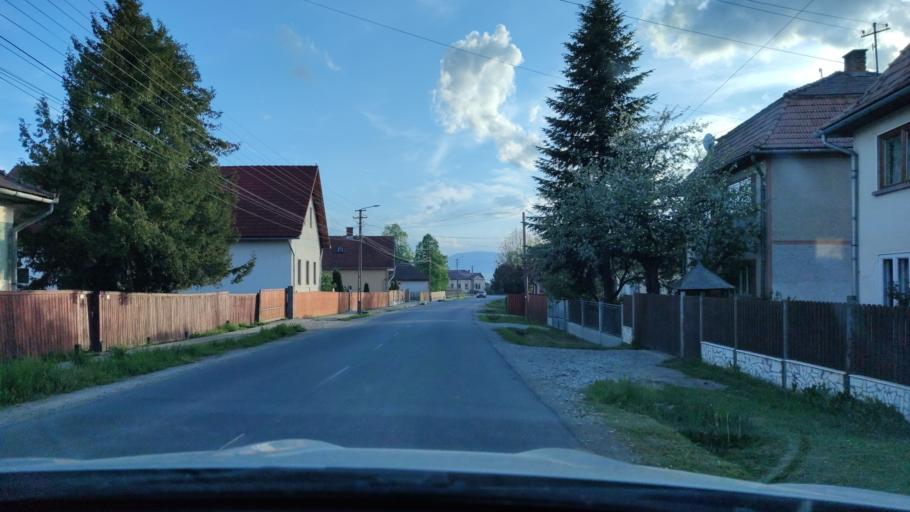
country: RO
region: Harghita
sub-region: Comuna Ditrau
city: Ditrau
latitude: 46.8059
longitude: 25.4982
